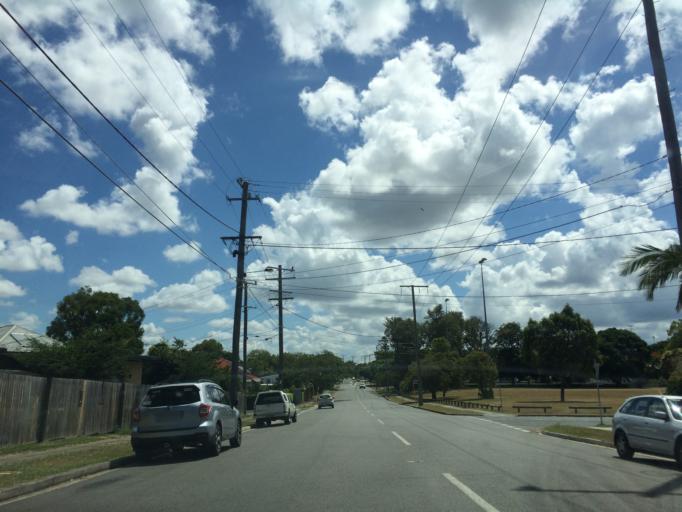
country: AU
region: Queensland
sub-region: Brisbane
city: Seven Hills
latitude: -27.4843
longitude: 153.0632
